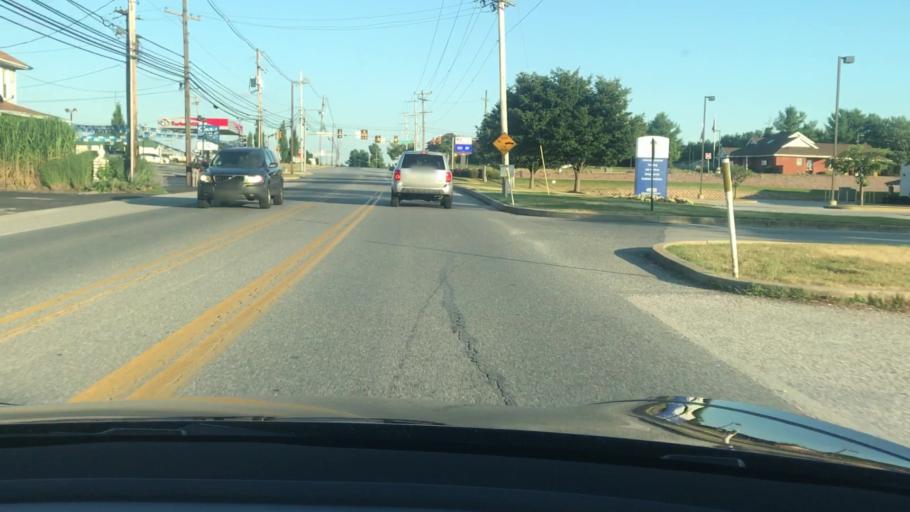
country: US
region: Pennsylvania
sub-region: York County
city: Dover
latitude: 39.9942
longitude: -76.8434
